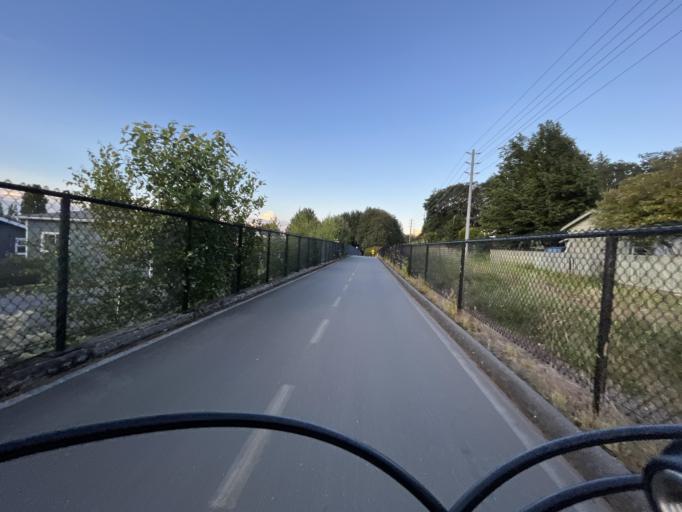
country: CA
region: British Columbia
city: Victoria
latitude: 48.4380
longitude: -123.4090
